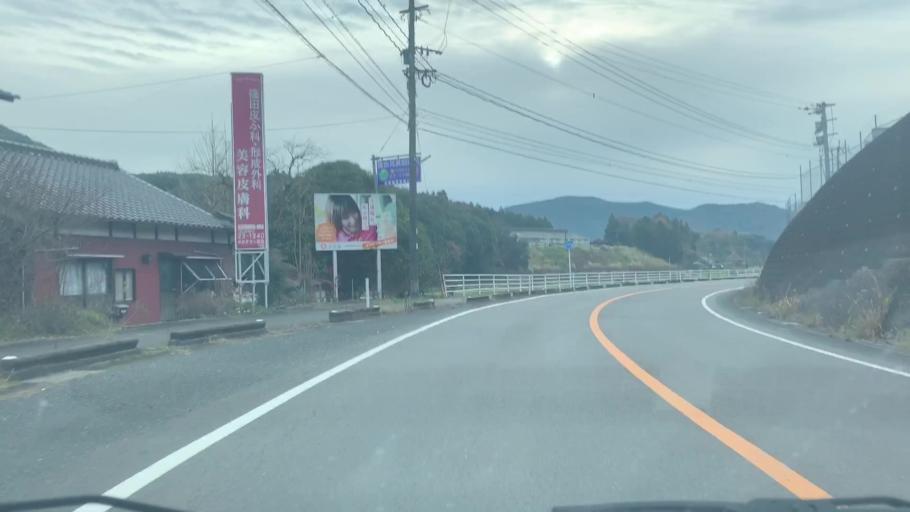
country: JP
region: Saga Prefecture
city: Takeocho-takeo
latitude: 33.1660
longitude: 130.0586
